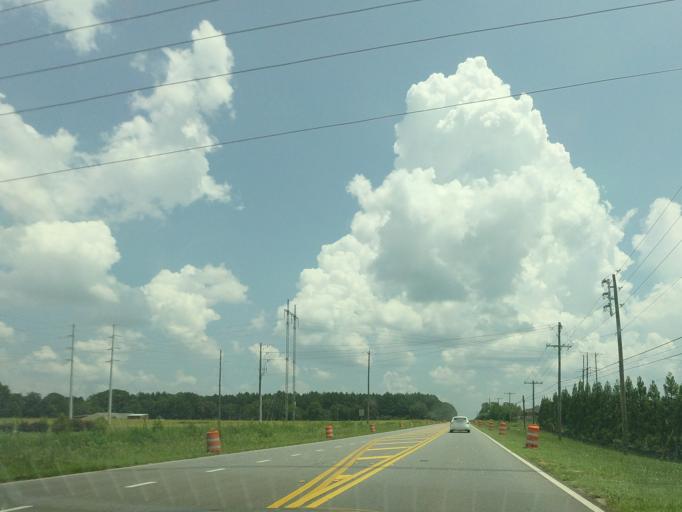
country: US
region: Georgia
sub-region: Houston County
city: Robins Air Force Base
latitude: 32.5437
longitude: -83.5837
